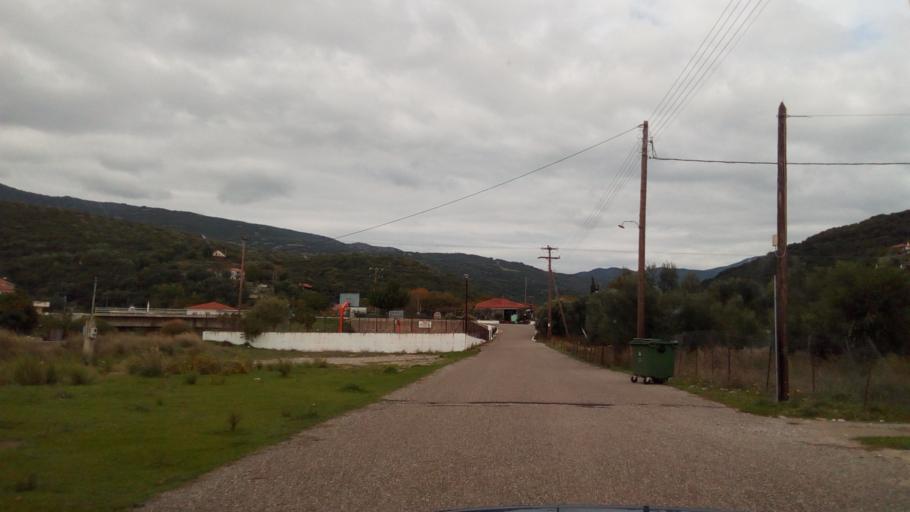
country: GR
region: West Greece
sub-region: Nomos Achaias
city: Kamarai
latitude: 38.4207
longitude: 21.9591
